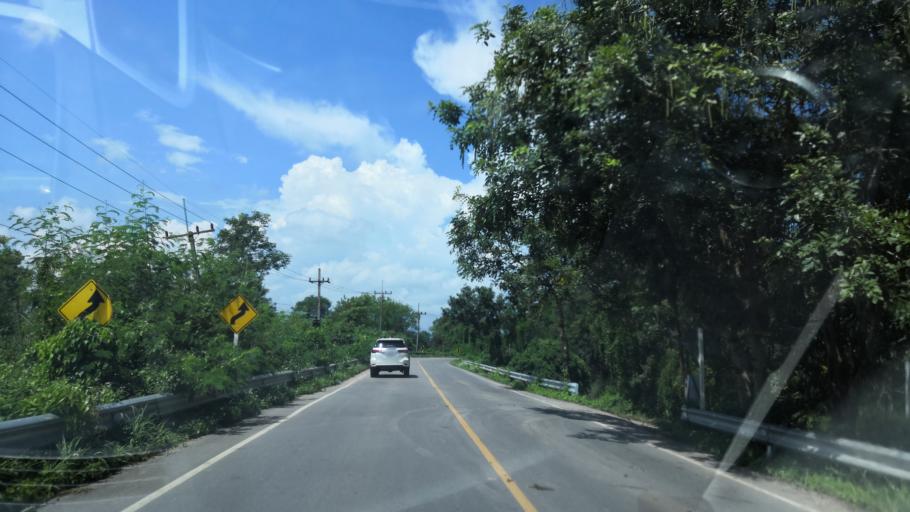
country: TH
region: Chiang Rai
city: Wiang Chiang Rung
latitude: 19.9704
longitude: 99.9800
